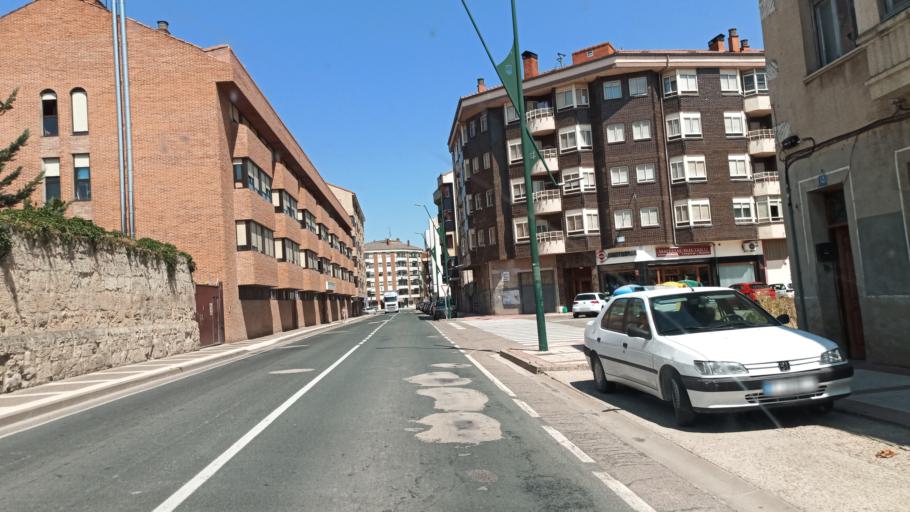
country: ES
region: Castille and Leon
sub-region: Provincia de Burgos
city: Briviesca
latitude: 42.5493
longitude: -3.3212
